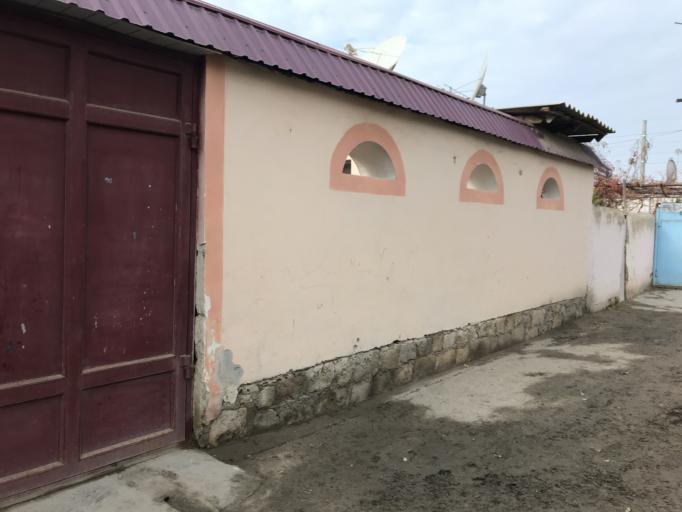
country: UZ
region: Bukhara
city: Kogon
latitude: 39.7244
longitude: 64.5541
